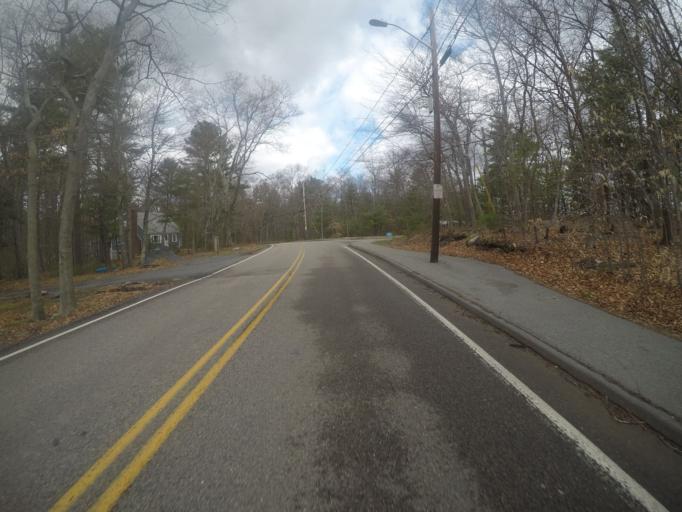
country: US
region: Massachusetts
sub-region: Bristol County
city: Easton
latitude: 42.0514
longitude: -71.1120
